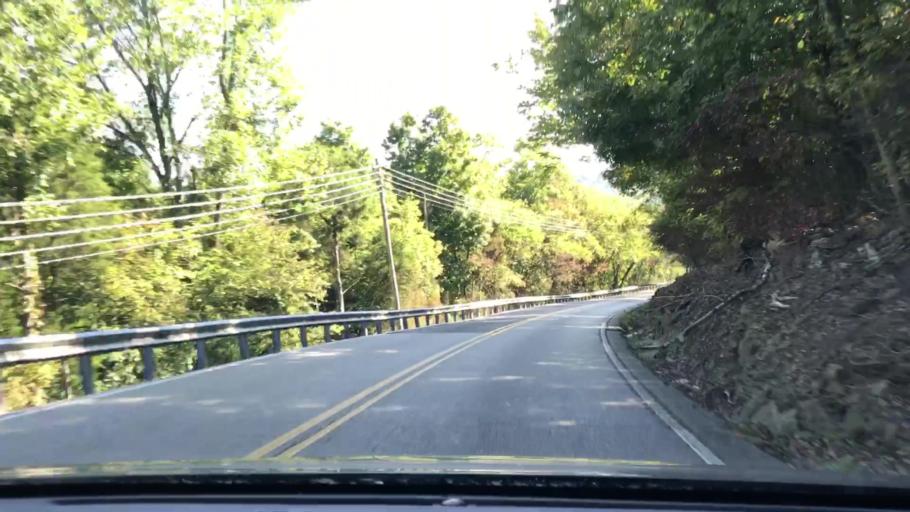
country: US
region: Tennessee
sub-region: Jackson County
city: Gainesboro
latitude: 36.3551
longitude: -85.6638
